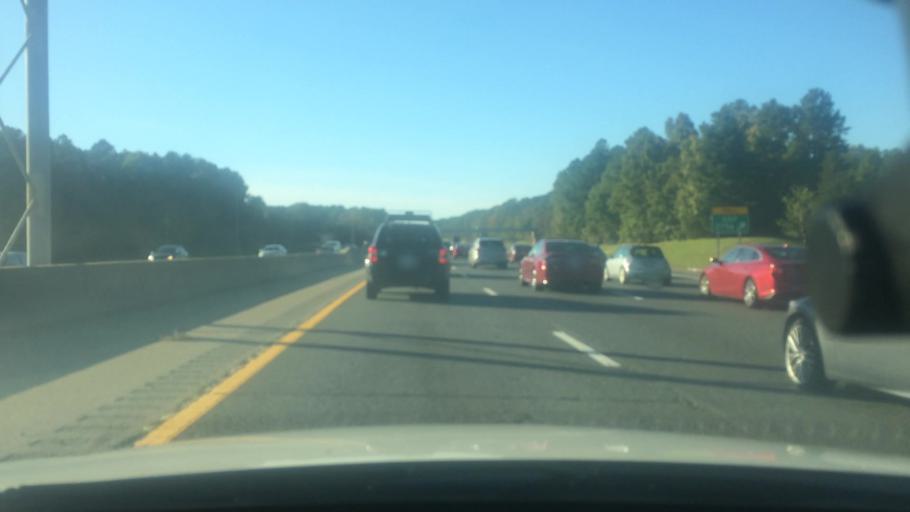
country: US
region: North Carolina
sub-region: Wake County
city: Morrisville
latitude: 35.9010
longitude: -78.8757
